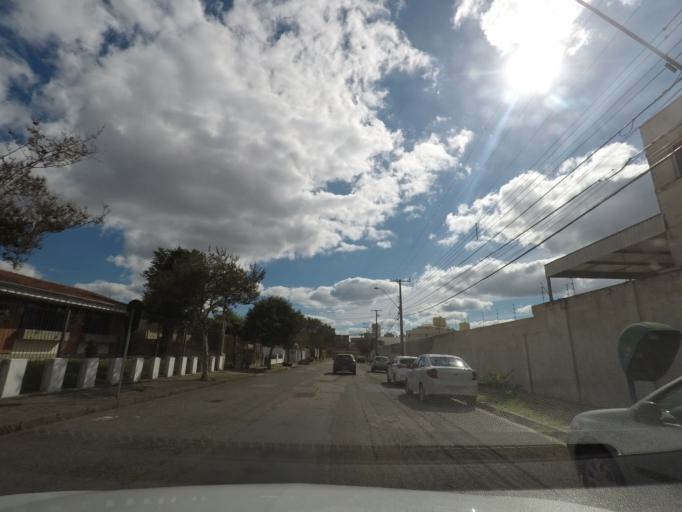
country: BR
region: Parana
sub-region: Curitiba
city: Curitiba
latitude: -25.4391
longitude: -49.2433
